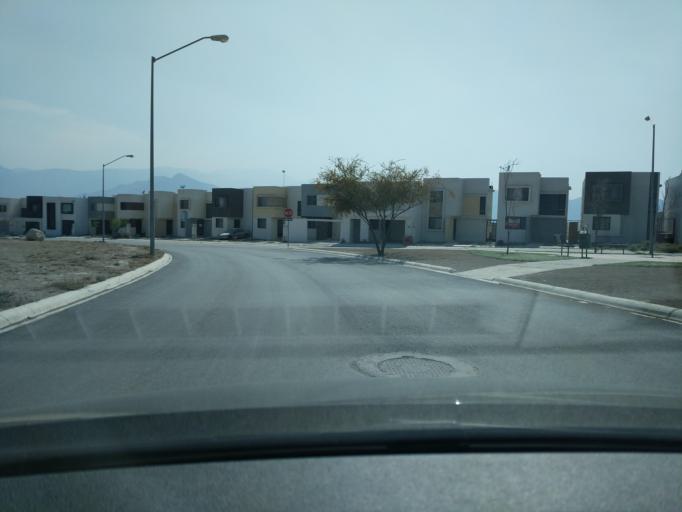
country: MX
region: Nuevo Leon
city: Garcia
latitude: 25.8160
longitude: -100.5413
